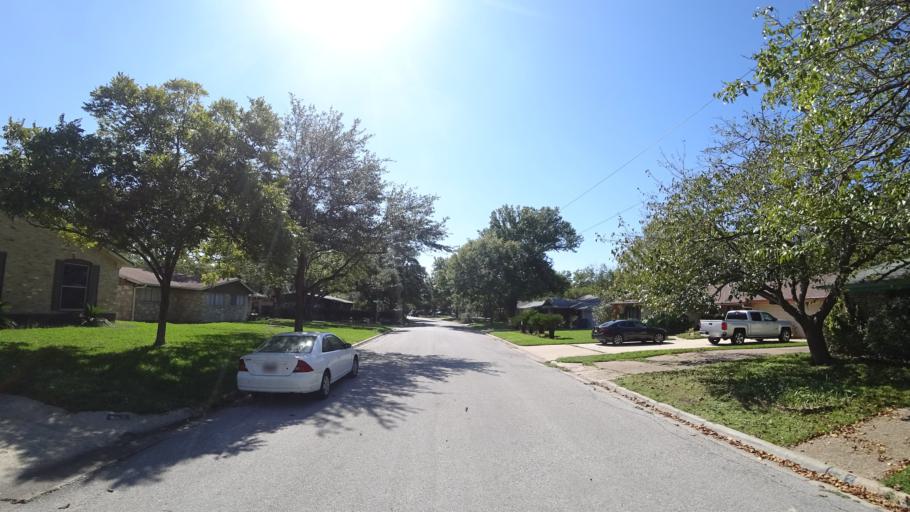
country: US
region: Texas
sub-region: Travis County
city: Austin
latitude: 30.3107
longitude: -97.6931
